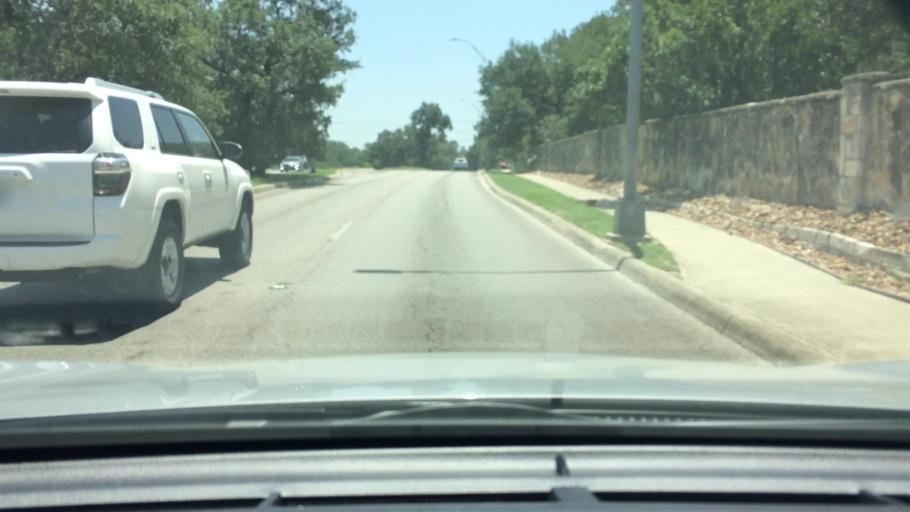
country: US
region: Texas
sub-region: Bexar County
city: Shavano Park
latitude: 29.5609
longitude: -98.5828
